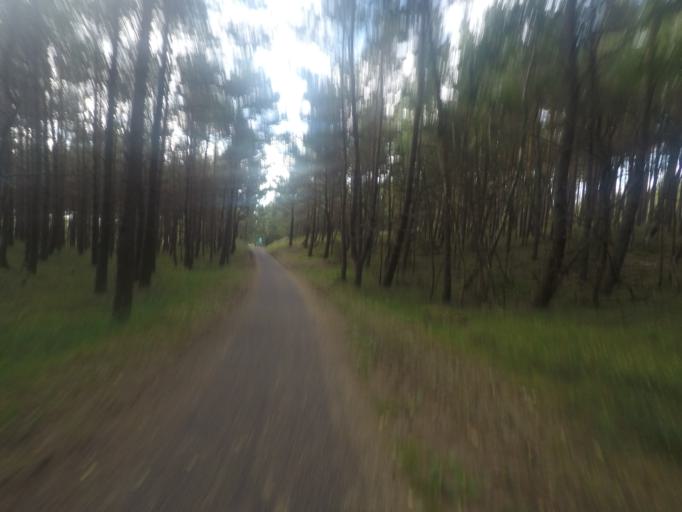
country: LT
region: Klaipedos apskritis
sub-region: Klaipeda
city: Klaipeda
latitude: 55.6521
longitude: 21.1084
